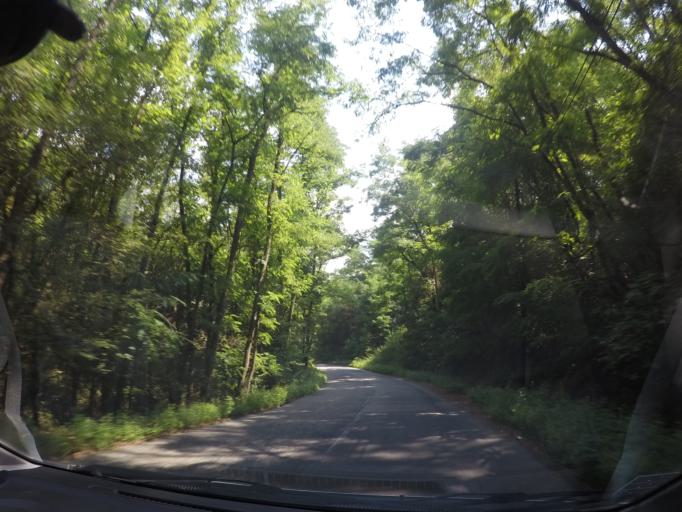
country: SK
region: Nitriansky
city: Levice
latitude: 48.2429
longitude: 18.6892
